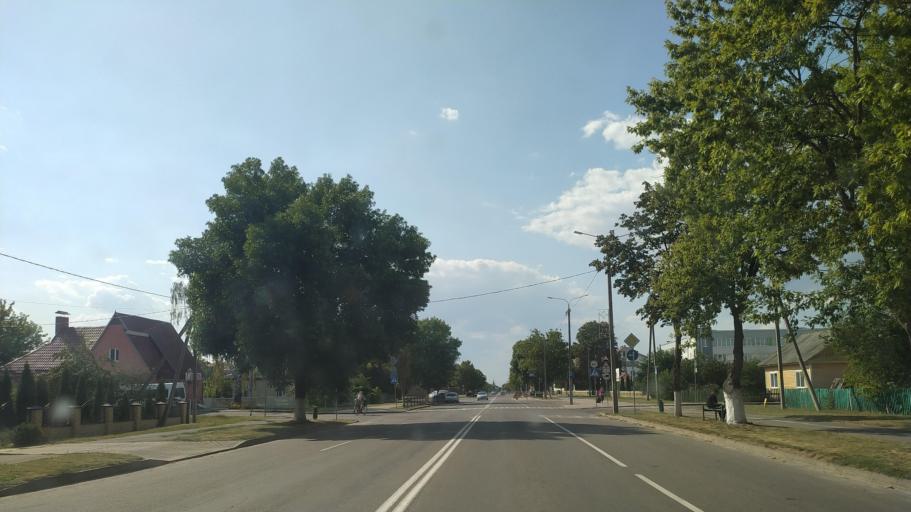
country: BY
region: Brest
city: Drahichyn
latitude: 52.1848
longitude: 25.1669
